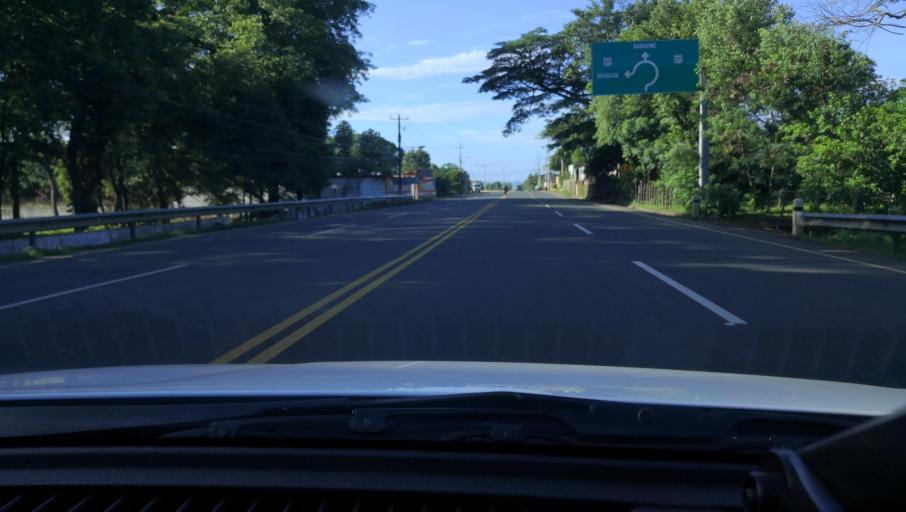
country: NI
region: Granada
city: Nandaime
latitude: 11.7795
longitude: -86.0543
